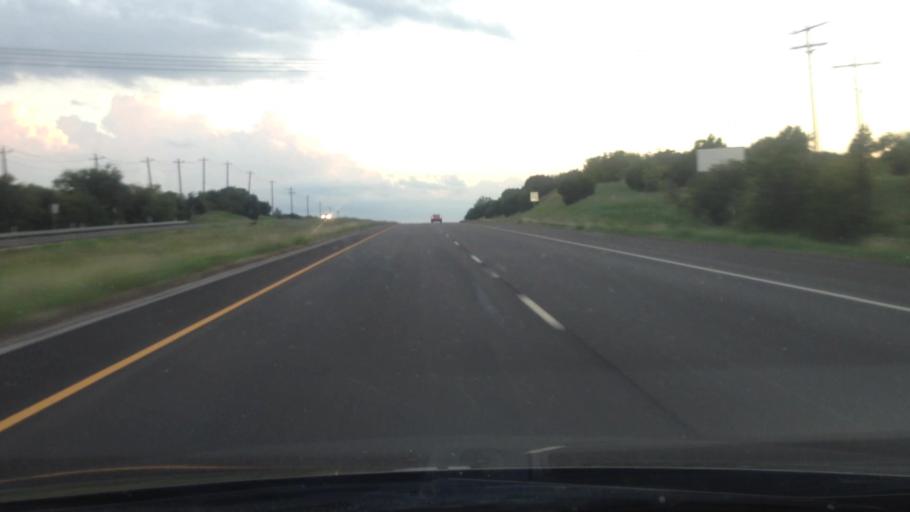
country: US
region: Texas
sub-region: Hood County
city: DeCordova
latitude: 32.5179
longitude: -97.6298
